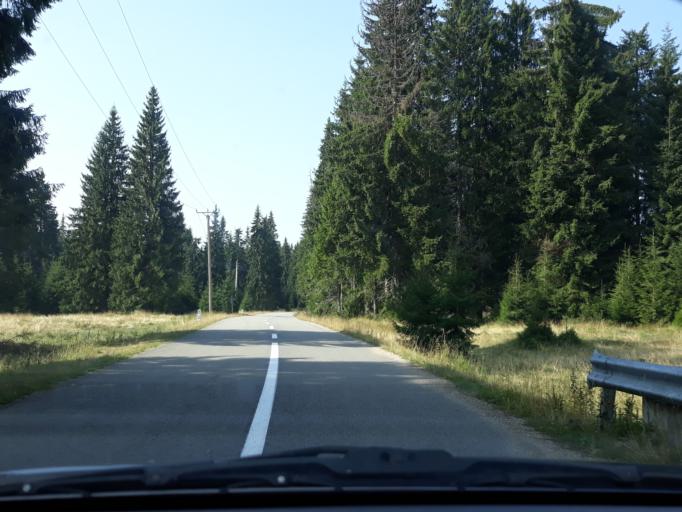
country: RO
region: Alba
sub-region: Comuna Arieseni
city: Arieseni
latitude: 46.5969
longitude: 22.7075
